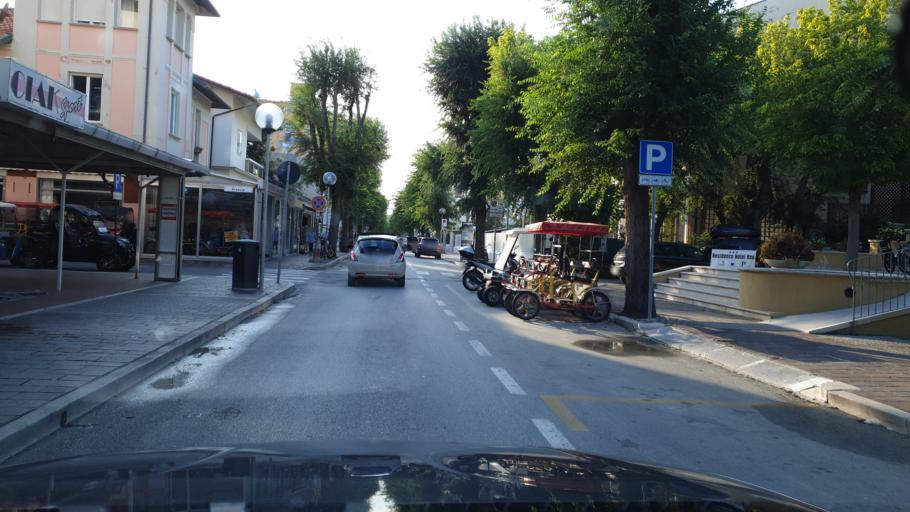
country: IT
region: Emilia-Romagna
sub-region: Provincia di Rimini
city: Cattolica
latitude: 43.9669
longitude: 12.7364
